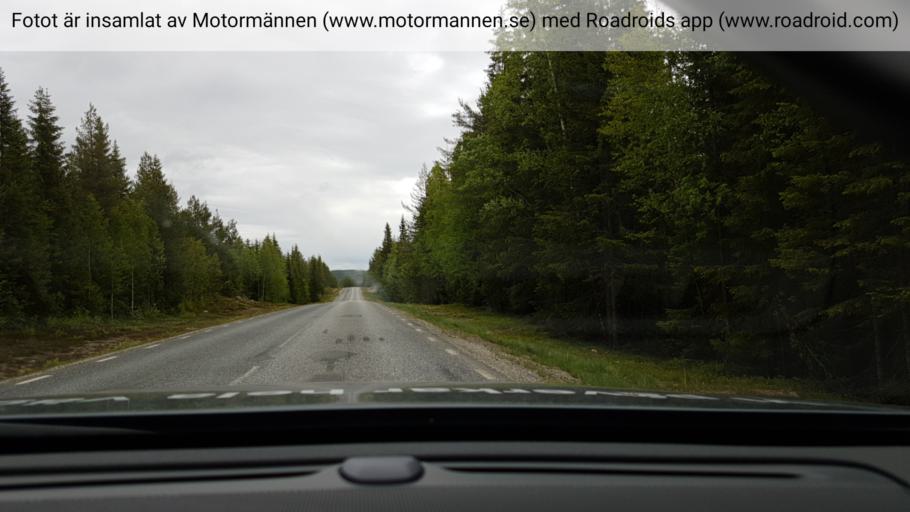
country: SE
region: Vaesterbotten
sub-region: Asele Kommun
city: Insjon
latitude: 64.3475
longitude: 17.8711
